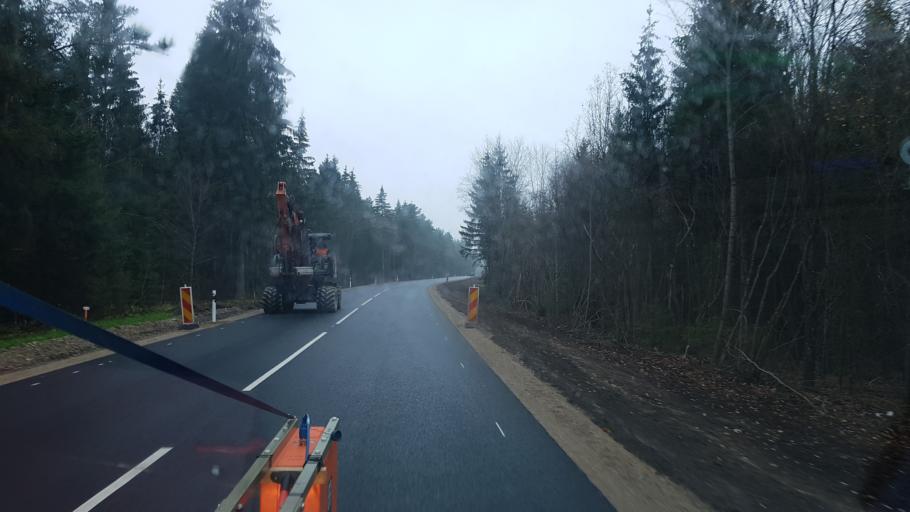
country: EE
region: Raplamaa
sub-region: Kohila vald
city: Kohila
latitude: 59.1777
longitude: 24.7905
